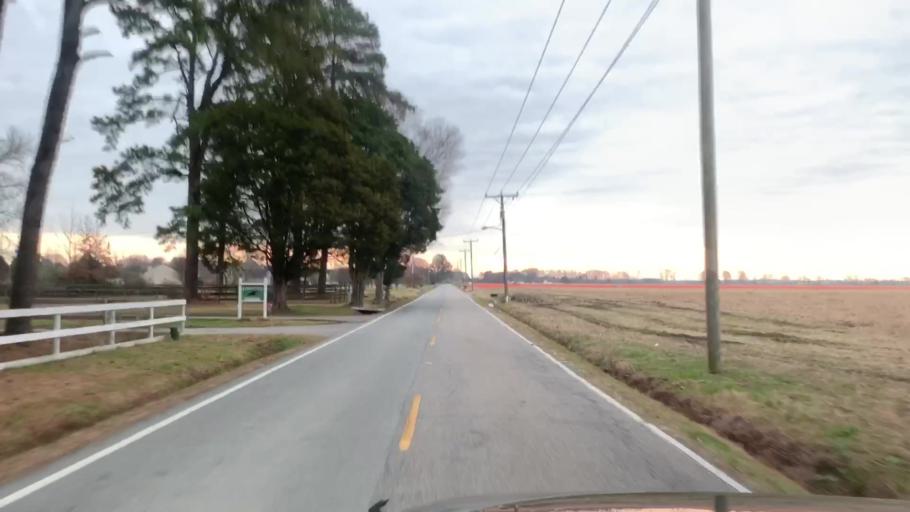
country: US
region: North Carolina
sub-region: Currituck County
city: Moyock
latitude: 36.6302
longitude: -76.1750
